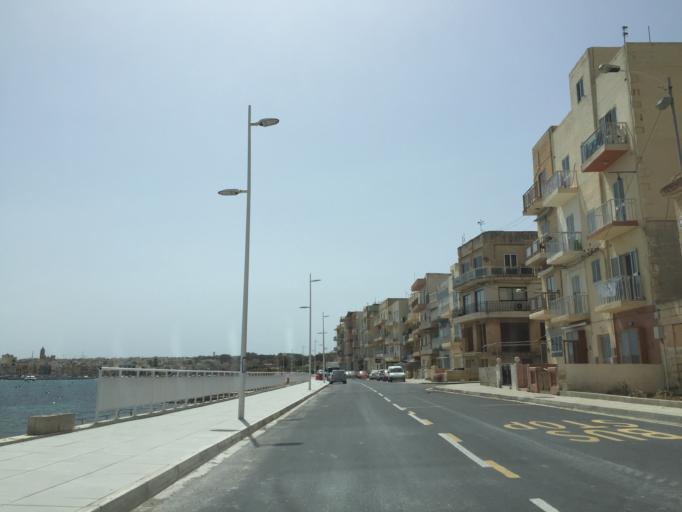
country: MT
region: Marsaxlokk
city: Marsaxlokk
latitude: 35.8330
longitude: 14.5371
